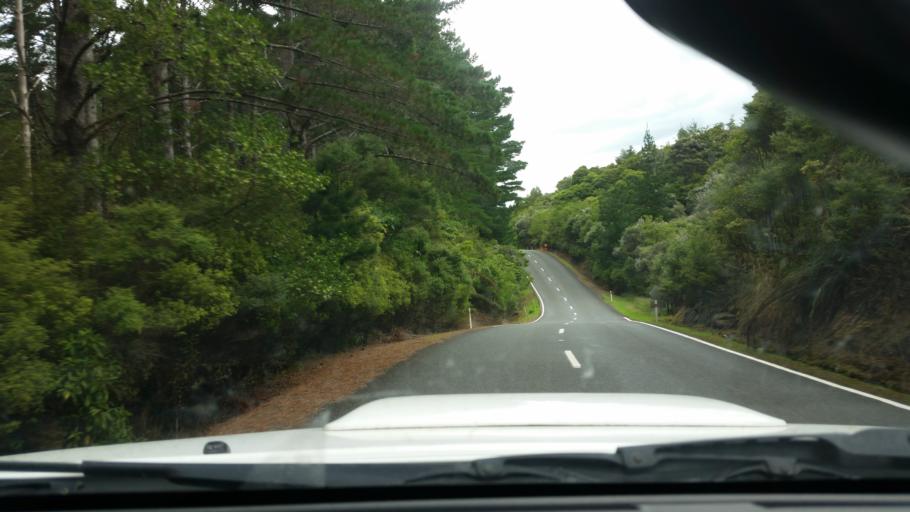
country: NZ
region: Northland
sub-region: Kaipara District
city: Dargaville
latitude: -35.7318
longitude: 173.8631
